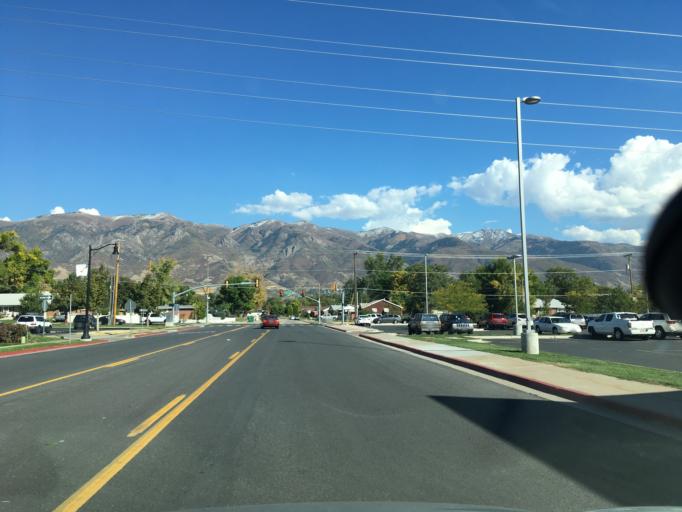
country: US
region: Utah
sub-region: Davis County
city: Layton
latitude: 41.0662
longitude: -111.9588
